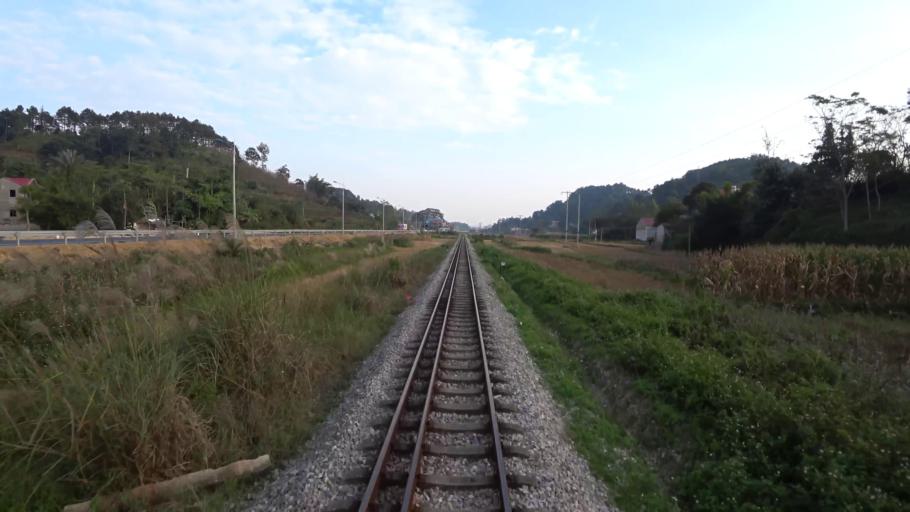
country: VN
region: Lang Son
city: Thi Tran Cao Loc
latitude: 21.9043
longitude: 106.7362
